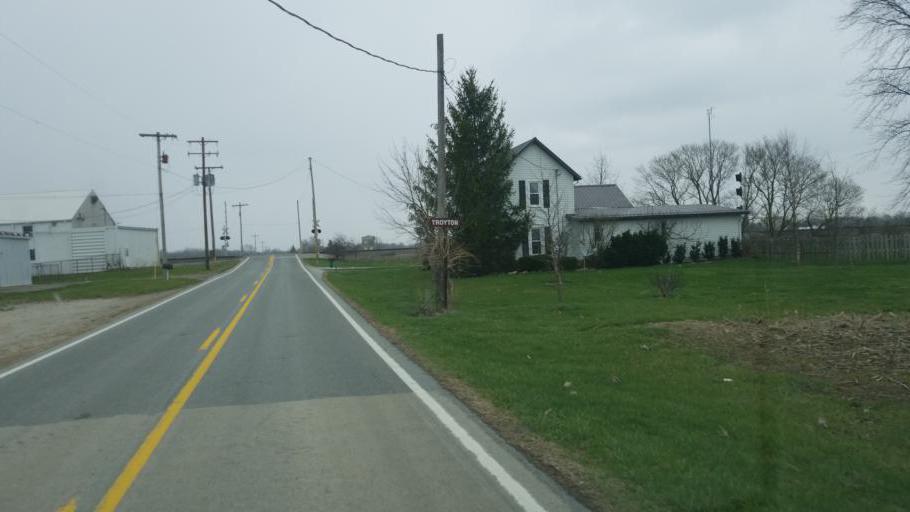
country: US
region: Ohio
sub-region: Delaware County
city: Delaware
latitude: 40.3943
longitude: -83.0817
